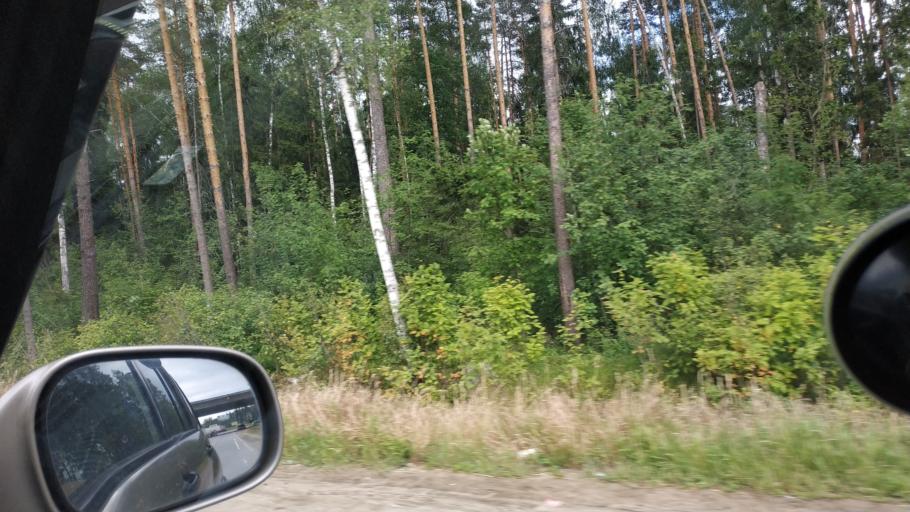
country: RU
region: Moskovskaya
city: Krasnoarmeysk
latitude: 56.0401
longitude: 38.1993
